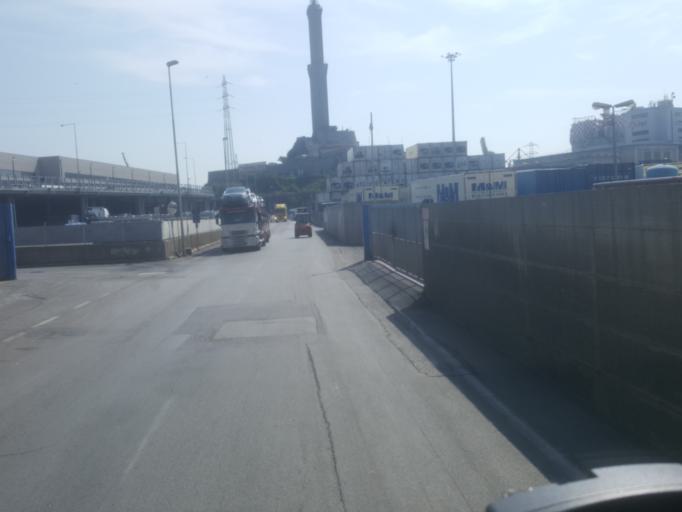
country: IT
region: Liguria
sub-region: Provincia di Genova
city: San Teodoro
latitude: 44.4056
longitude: 8.9002
